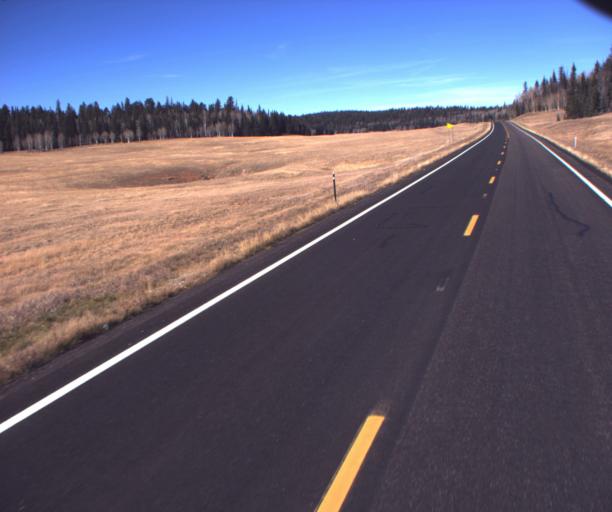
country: US
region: Arizona
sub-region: Coconino County
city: Grand Canyon
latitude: 36.4311
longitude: -112.1326
